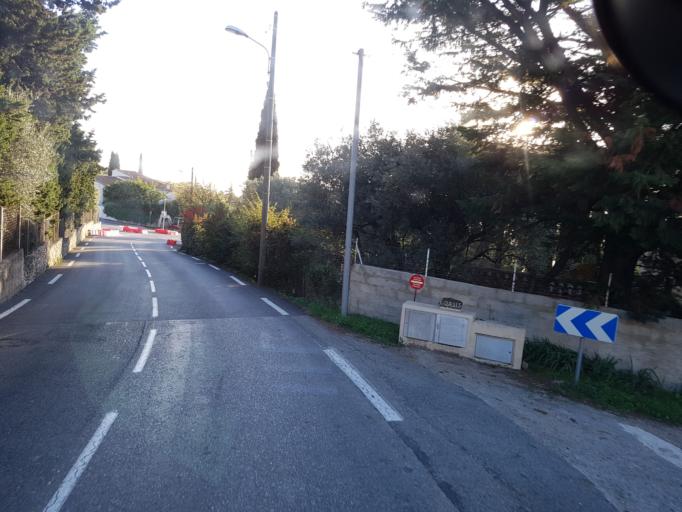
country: FR
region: Provence-Alpes-Cote d'Azur
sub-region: Departement des Bouches-du-Rhone
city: Ceyreste
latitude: 43.2196
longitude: 5.6401
